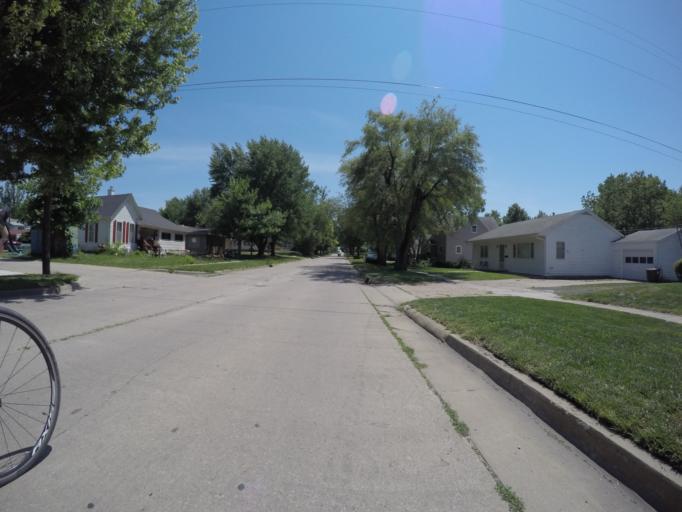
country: US
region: Kansas
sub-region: Nemaha County
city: Sabetha
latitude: 39.9021
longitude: -95.8072
